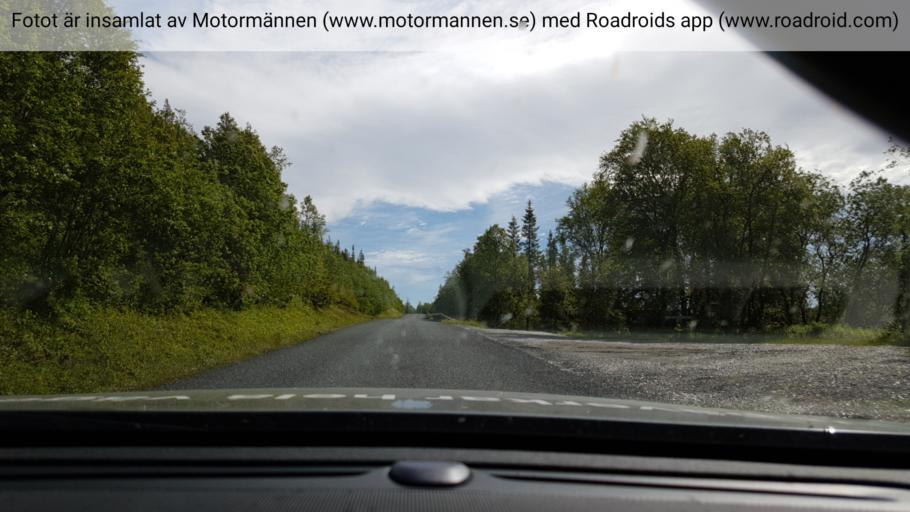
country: SE
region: Vaesterbotten
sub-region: Vilhelmina Kommun
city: Sjoberg
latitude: 65.2391
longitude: 15.4471
